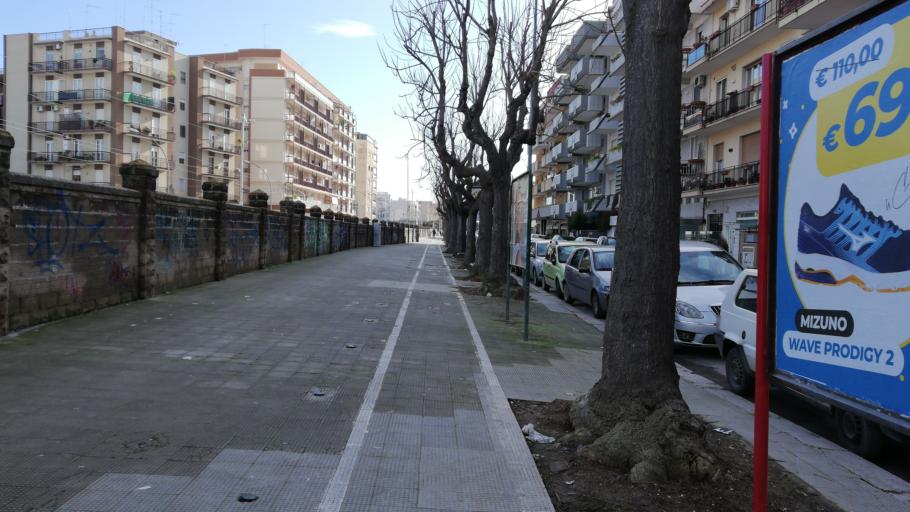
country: IT
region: Apulia
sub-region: Provincia di Barletta - Andria - Trani
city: Andria
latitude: 41.2319
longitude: 16.3020
